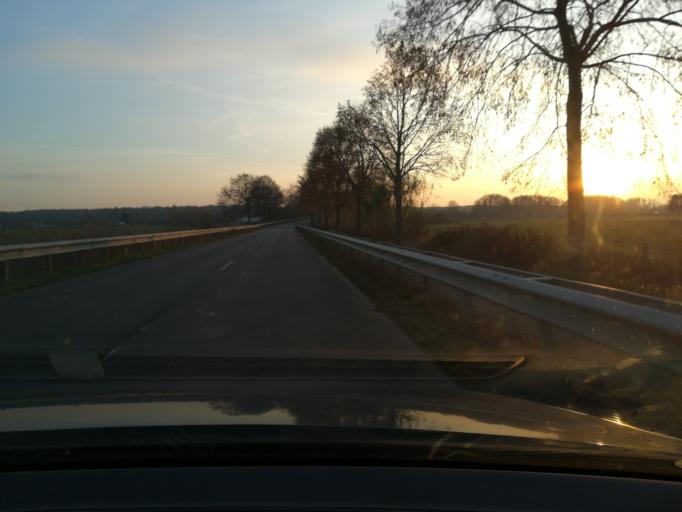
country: DE
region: Schleswig-Holstein
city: Escheburg
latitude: 53.4601
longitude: 10.3180
